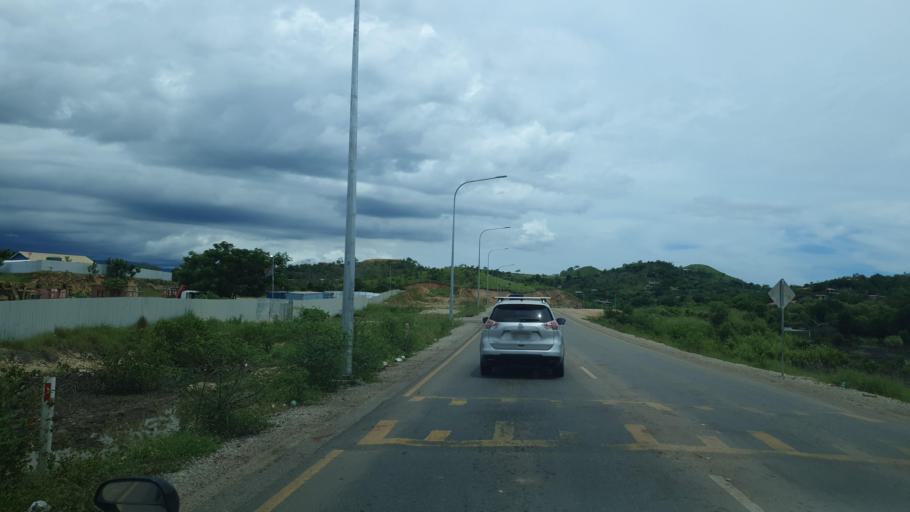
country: PG
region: National Capital
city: Port Moresby
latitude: -9.5051
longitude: 147.2371
